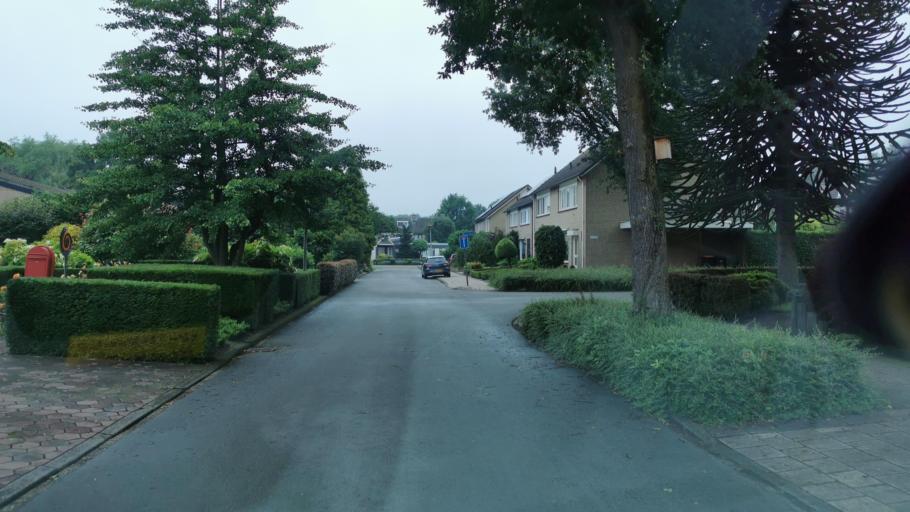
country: NL
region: Overijssel
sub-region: Gemeente Losser
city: Losser
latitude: 52.2545
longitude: 7.0072
